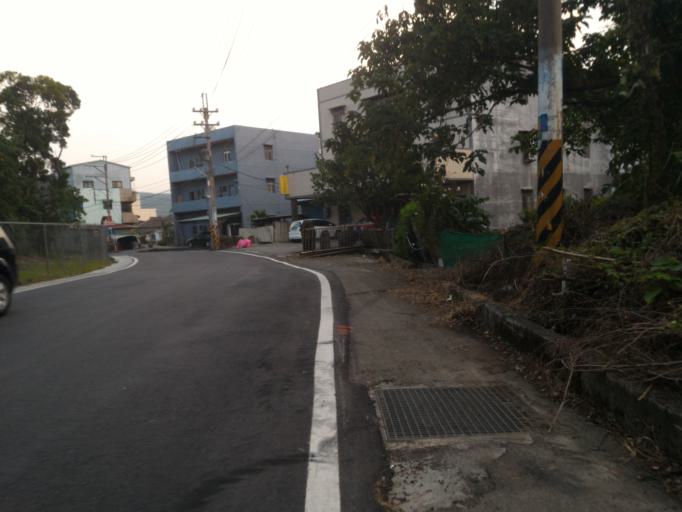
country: TW
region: Taiwan
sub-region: Taoyuan
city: Taoyuan
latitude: 24.9506
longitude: 121.3924
